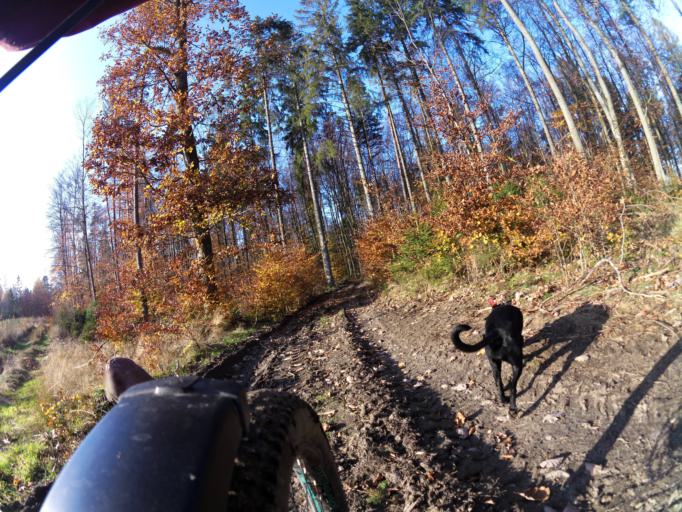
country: PL
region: Pomeranian Voivodeship
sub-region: Powiat pucki
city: Krokowa
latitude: 54.7280
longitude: 18.2154
